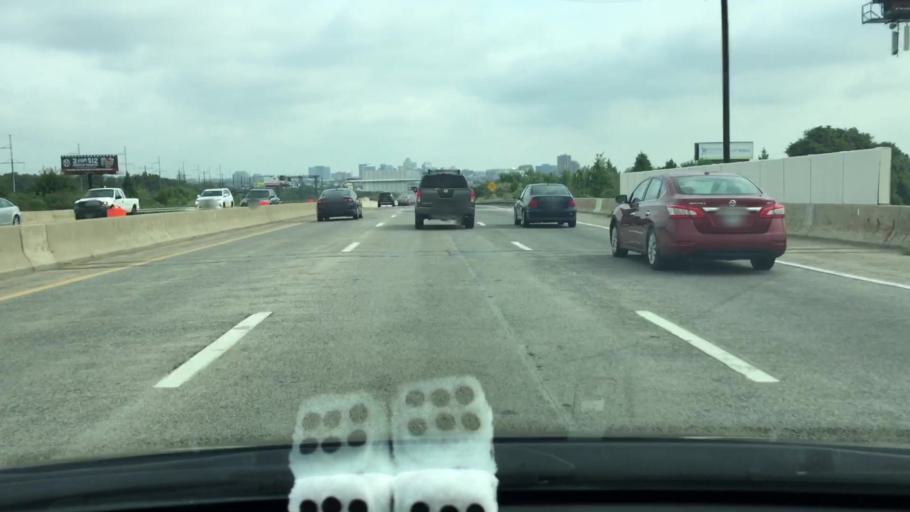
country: US
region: Delaware
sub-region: New Castle County
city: Elsmere
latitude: 39.7206
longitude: -75.5774
